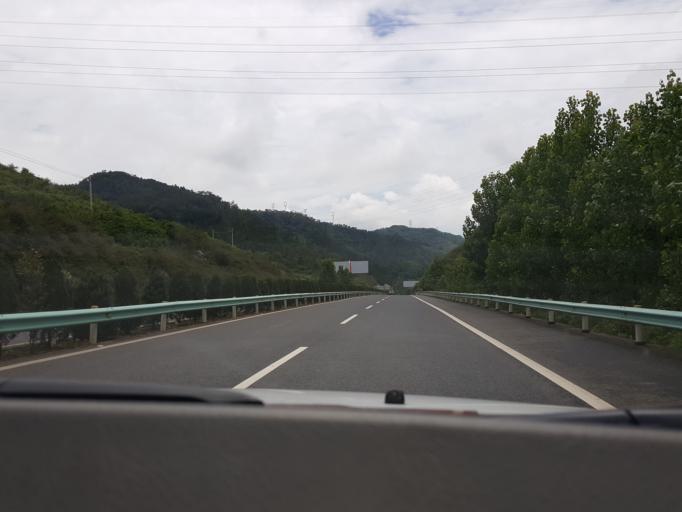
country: CN
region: Guangxi Zhuangzu Zizhiqu
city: Xinzhou
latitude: 25.1899
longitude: 105.0218
